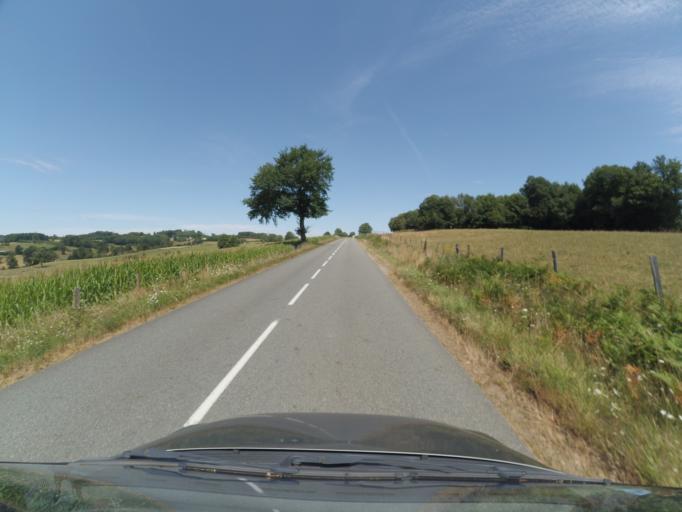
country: FR
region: Limousin
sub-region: Departement de la Creuse
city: Le Grand-Bourg
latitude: 46.1072
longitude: 1.6737
